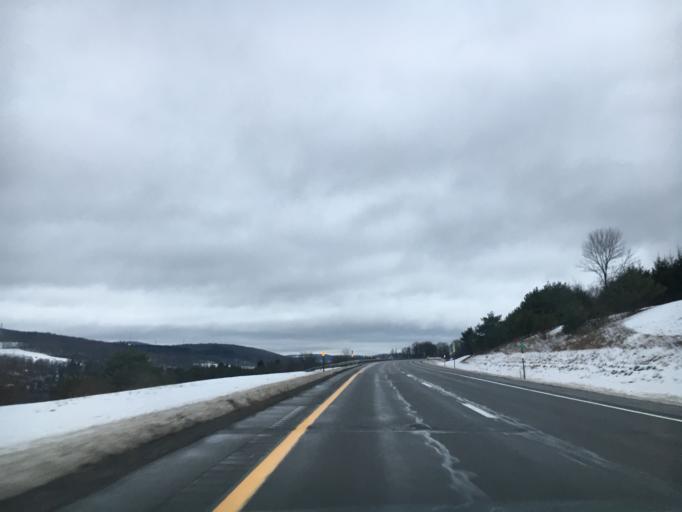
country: US
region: New York
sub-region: Cortland County
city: McGraw
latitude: 42.5623
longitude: -76.1135
